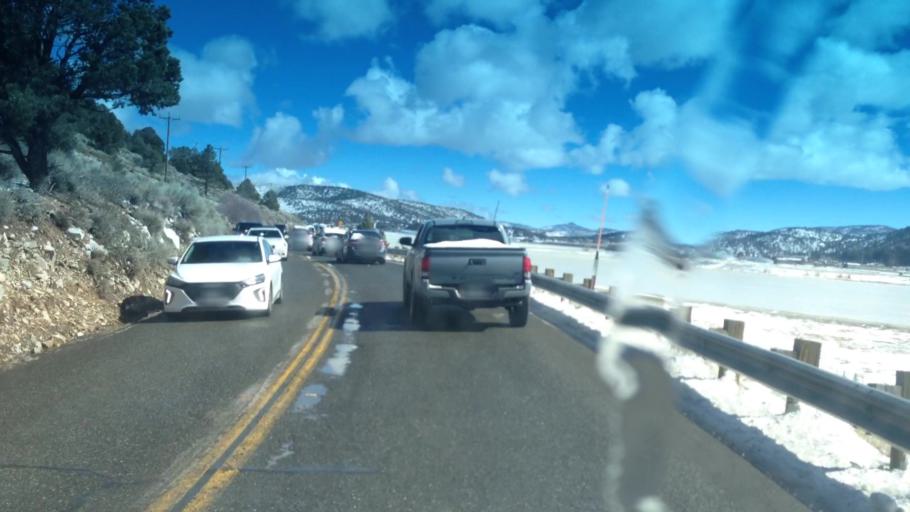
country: US
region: California
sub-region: San Bernardino County
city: Big Bear City
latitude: 34.2723
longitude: -116.8246
